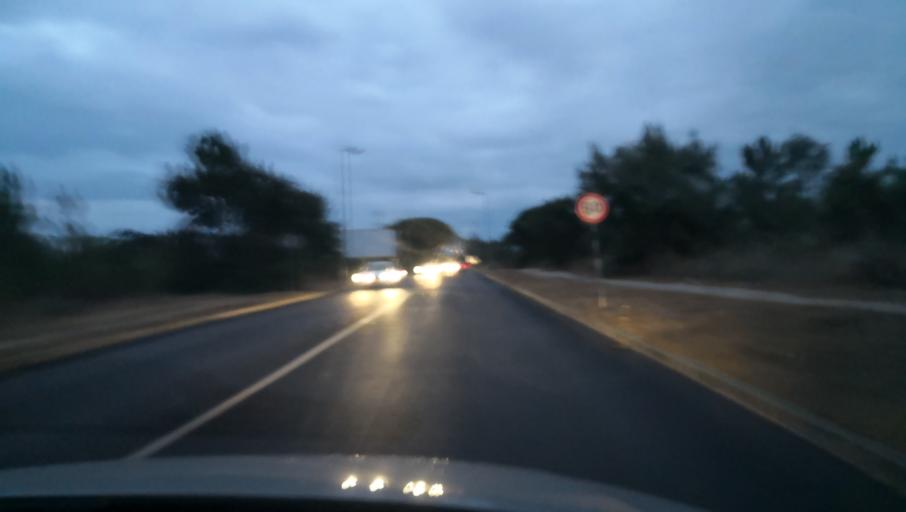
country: PT
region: Setubal
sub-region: Seixal
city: Amora
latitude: 38.6055
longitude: -9.1341
